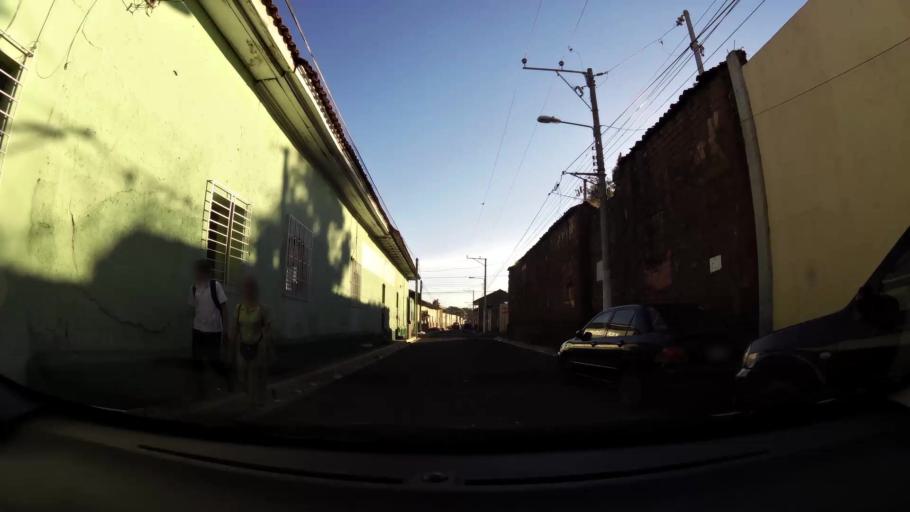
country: SV
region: San Miguel
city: San Miguel
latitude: 13.4867
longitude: -88.1769
